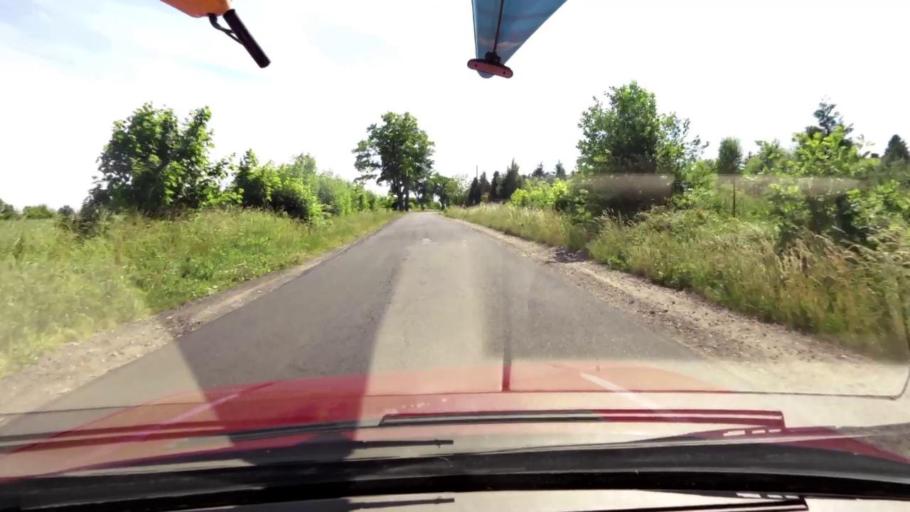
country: PL
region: Pomeranian Voivodeship
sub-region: Powiat slupski
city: Kobylnica
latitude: 54.4077
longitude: 17.0027
